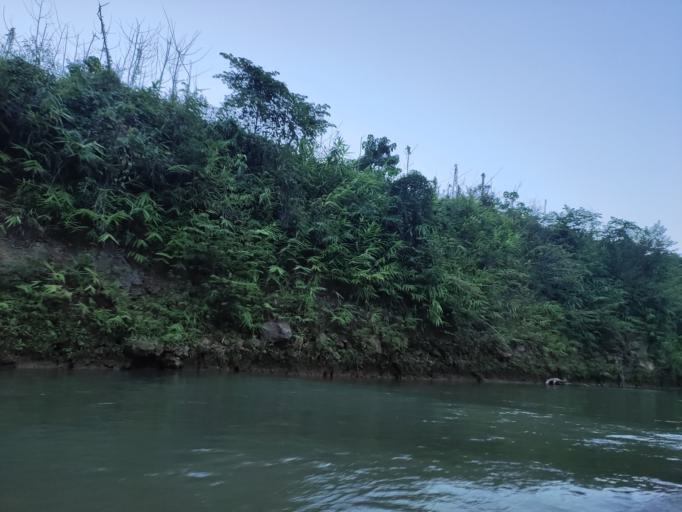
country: MM
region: Mandalay
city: Meiktila
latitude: 21.0215
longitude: 96.3874
